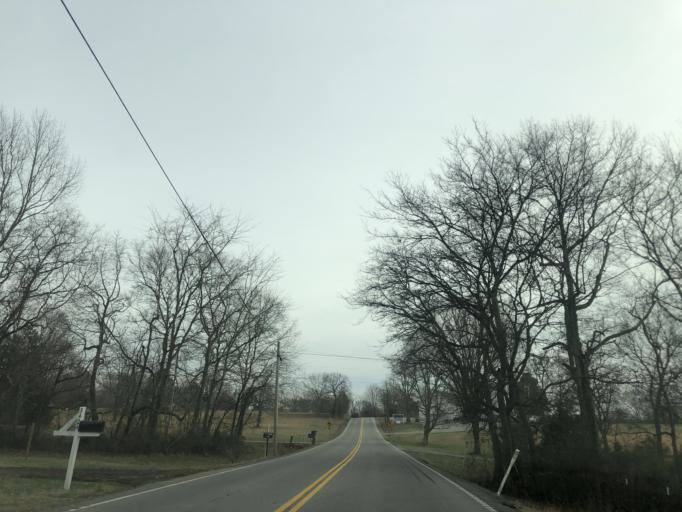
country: US
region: Tennessee
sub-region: Sumner County
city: White House
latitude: 36.5033
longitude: -86.6075
